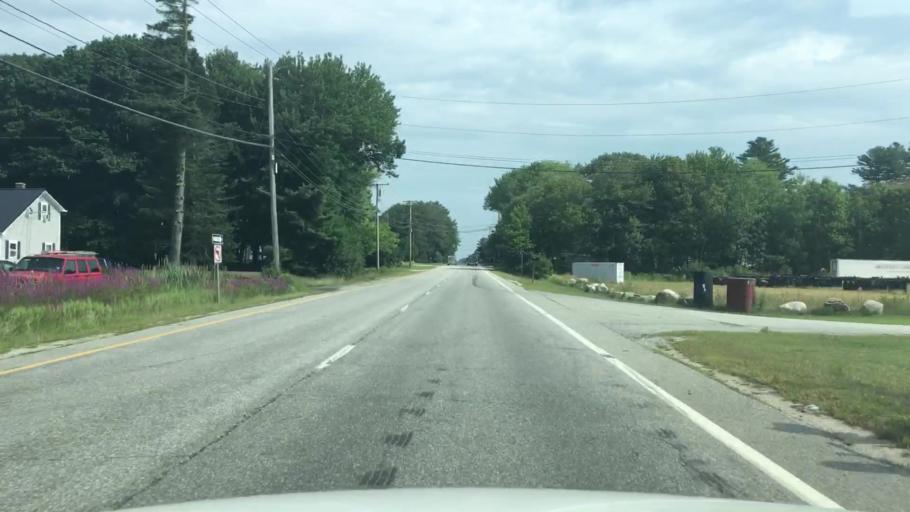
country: US
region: Maine
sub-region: Androscoggin County
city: Auburn
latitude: 44.0643
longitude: -70.2494
